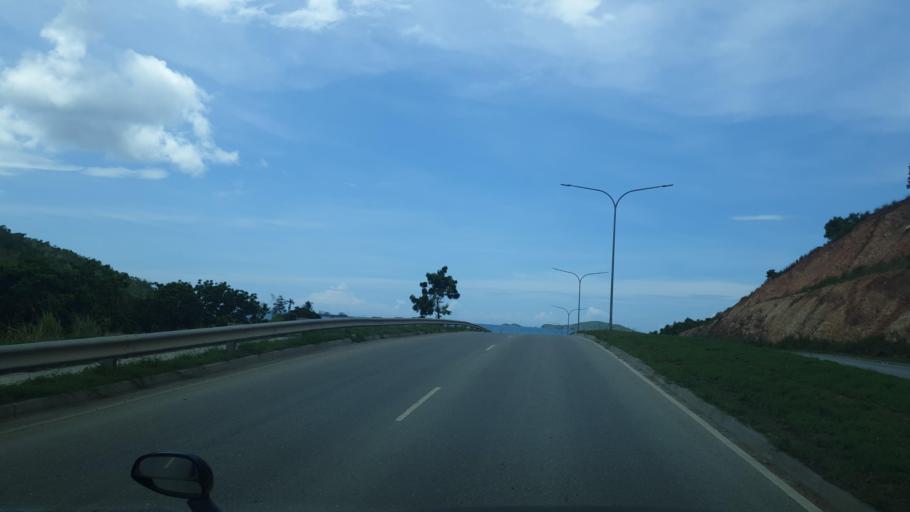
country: PG
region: National Capital
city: Port Moresby
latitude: -9.4345
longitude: 147.1399
